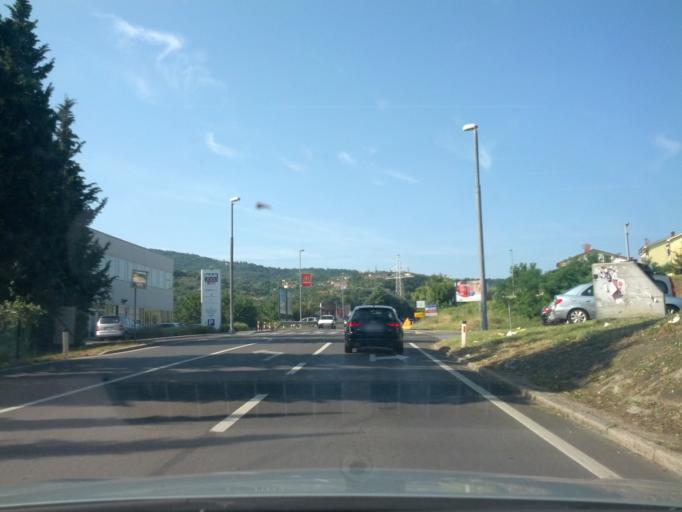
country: SI
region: Koper-Capodistria
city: Koper
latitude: 45.5273
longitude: 13.7347
